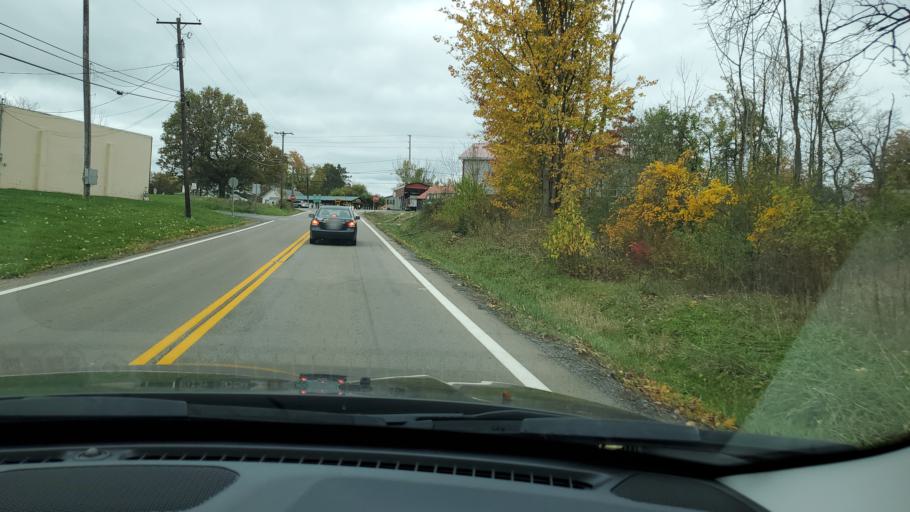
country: US
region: Ohio
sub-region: Columbiana County
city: East Palestine
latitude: 40.8665
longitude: -80.5598
